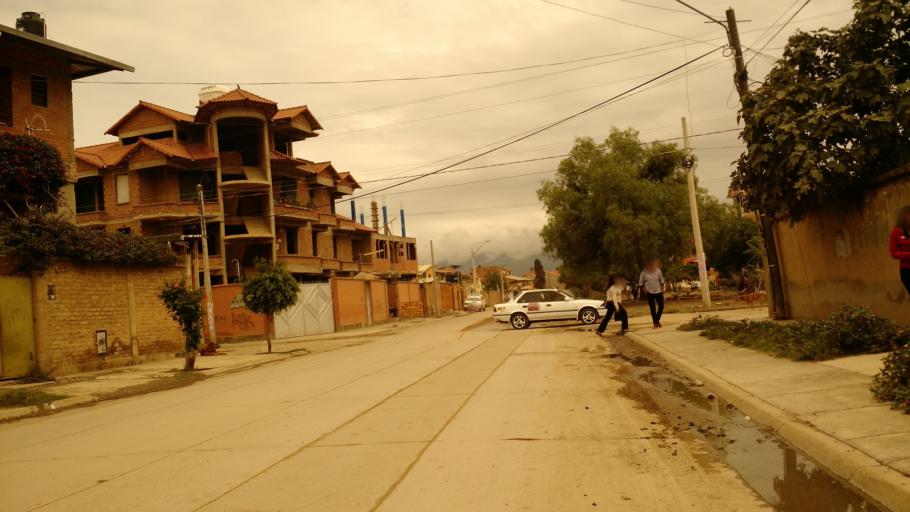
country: BO
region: Cochabamba
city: Cochabamba
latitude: -17.4380
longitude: -66.1546
